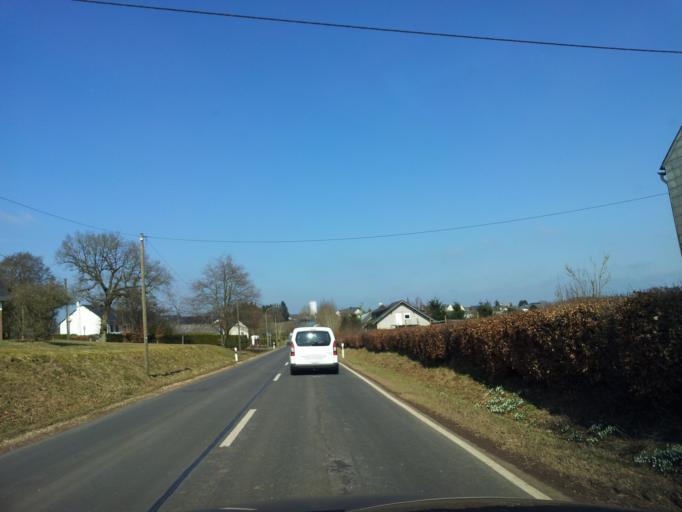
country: DE
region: Rheinland-Pfalz
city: Grosslangenfeld
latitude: 50.2162
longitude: 6.2525
